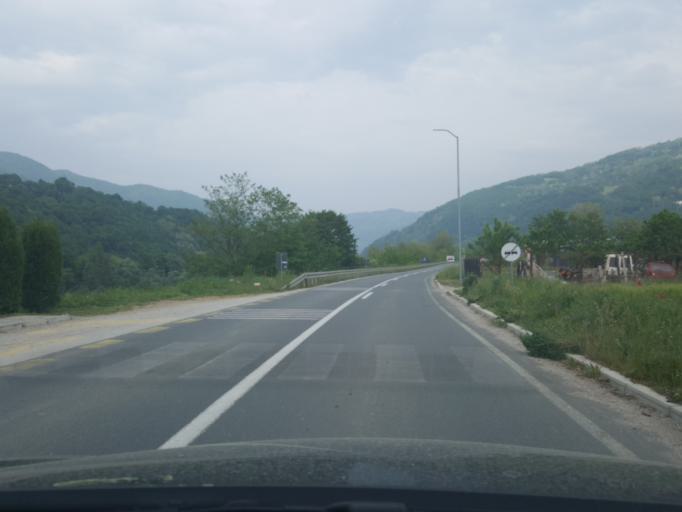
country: RS
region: Central Serbia
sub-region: Zlatiborski Okrug
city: Bajina Basta
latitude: 44.0002
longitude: 19.5724
